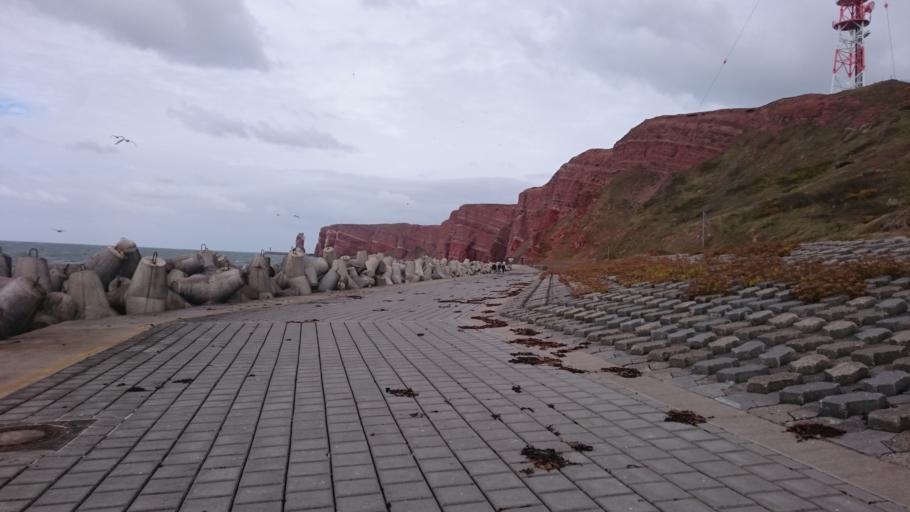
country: DE
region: Schleswig-Holstein
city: Helgoland
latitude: 54.1781
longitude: 7.8829
